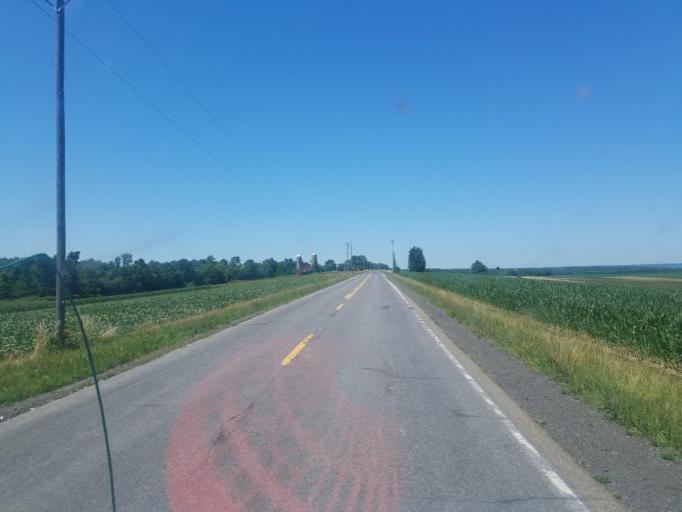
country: US
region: New York
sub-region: Yates County
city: Penn Yan
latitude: 42.7411
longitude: -77.0006
